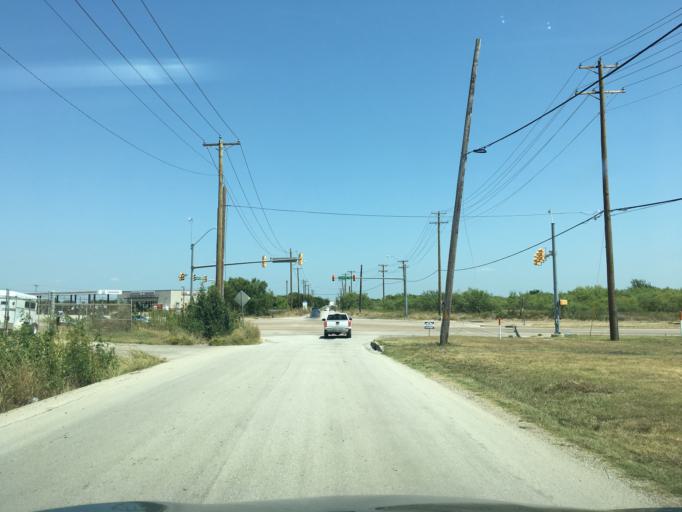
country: US
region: Texas
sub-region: Tarrant County
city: Crowley
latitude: 32.6142
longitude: -97.3512
